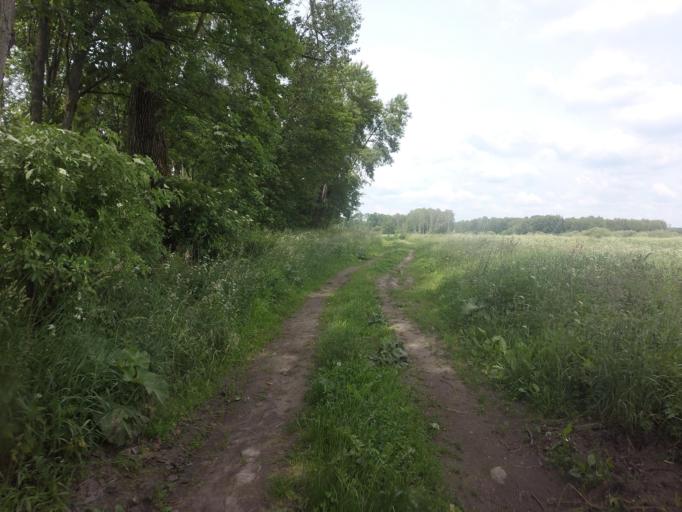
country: PL
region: West Pomeranian Voivodeship
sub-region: Powiat stargardzki
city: Dobrzany
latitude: 53.3006
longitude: 15.4743
